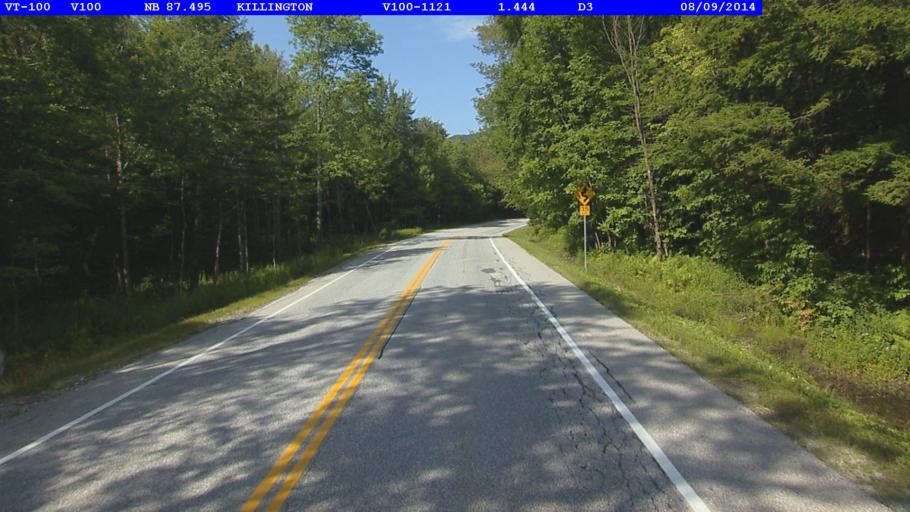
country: US
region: Vermont
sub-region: Rutland County
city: Rutland
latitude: 43.6867
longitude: -72.8133
